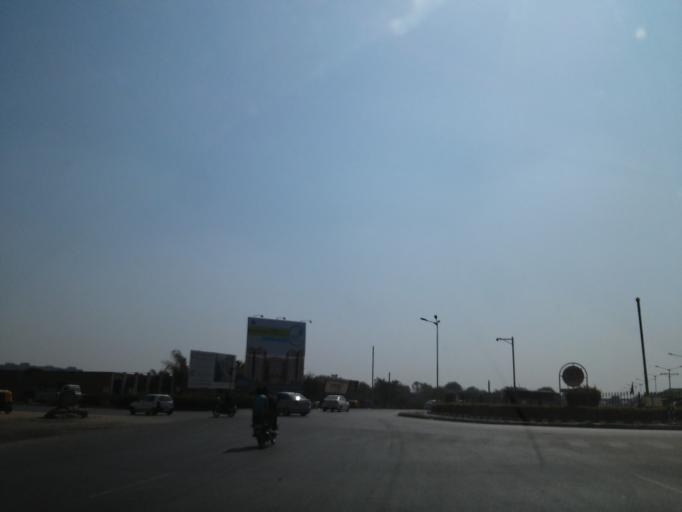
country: IN
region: Gujarat
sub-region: Gandhinagar
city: Adalaj
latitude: 23.1402
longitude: 72.5440
